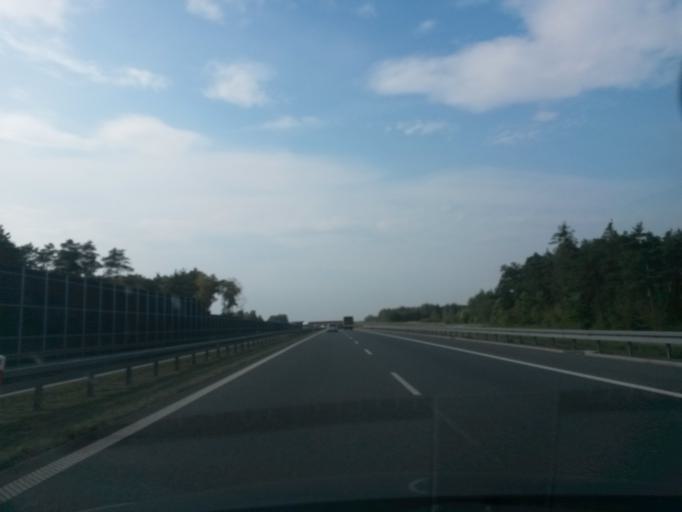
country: PL
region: Lesser Poland Voivodeship
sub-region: Powiat bochenski
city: Jodlowka
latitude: 49.9969
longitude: 20.5602
